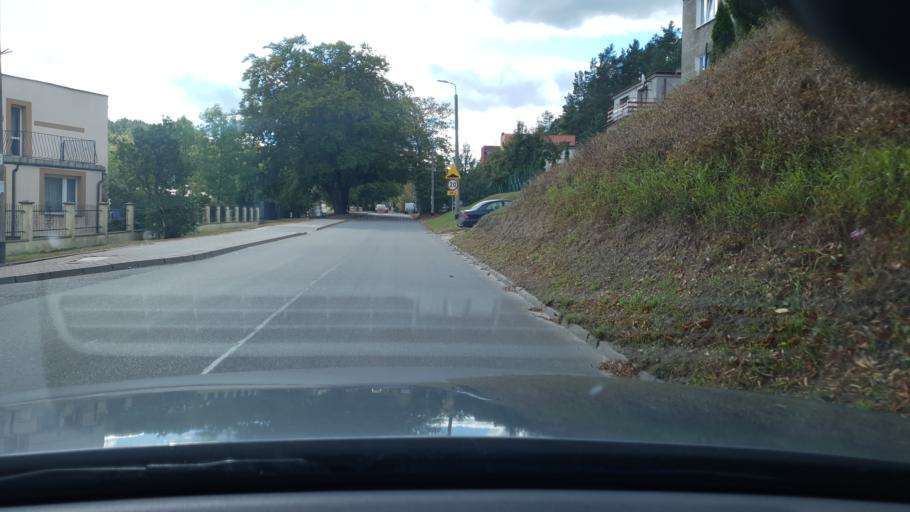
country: PL
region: Pomeranian Voivodeship
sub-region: Powiat wejherowski
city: Reda
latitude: 54.5973
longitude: 18.3452
